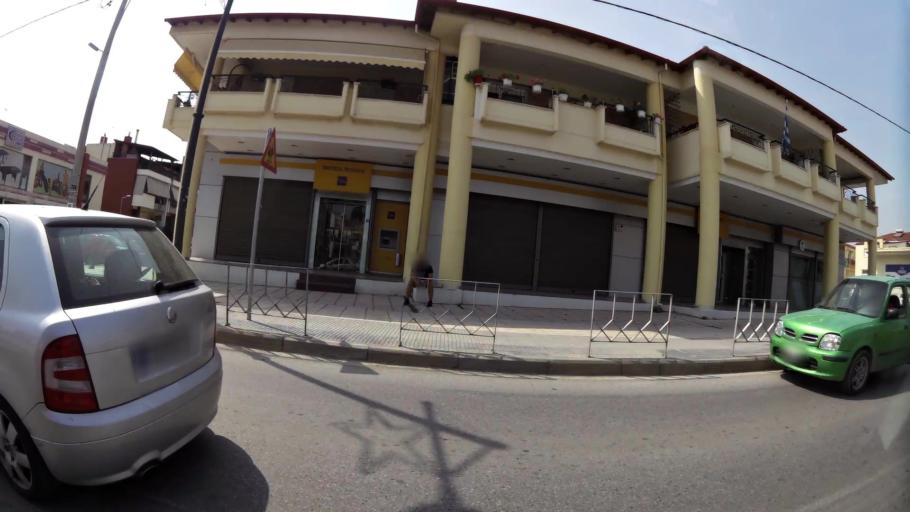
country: GR
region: Central Macedonia
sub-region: Nomos Thessalonikis
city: Efkarpia
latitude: 40.6826
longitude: 22.9488
